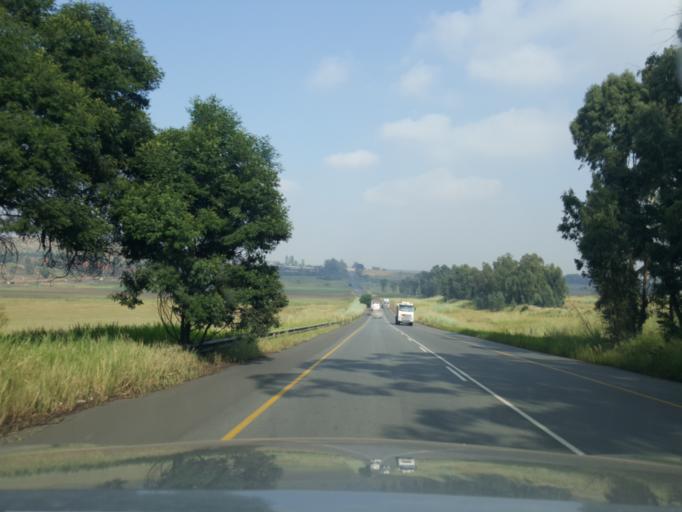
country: ZA
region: Mpumalanga
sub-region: Nkangala District Municipality
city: Witbank
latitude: -26.0141
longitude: 29.3752
